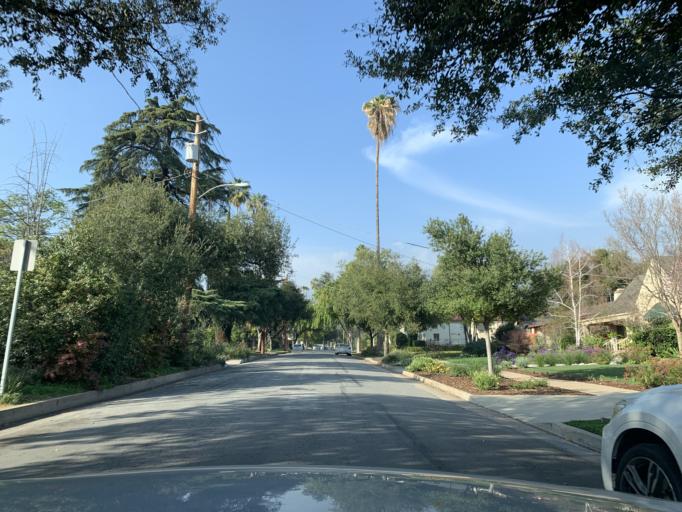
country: US
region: California
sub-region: Los Angeles County
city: Altadena
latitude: 34.1676
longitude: -118.1244
